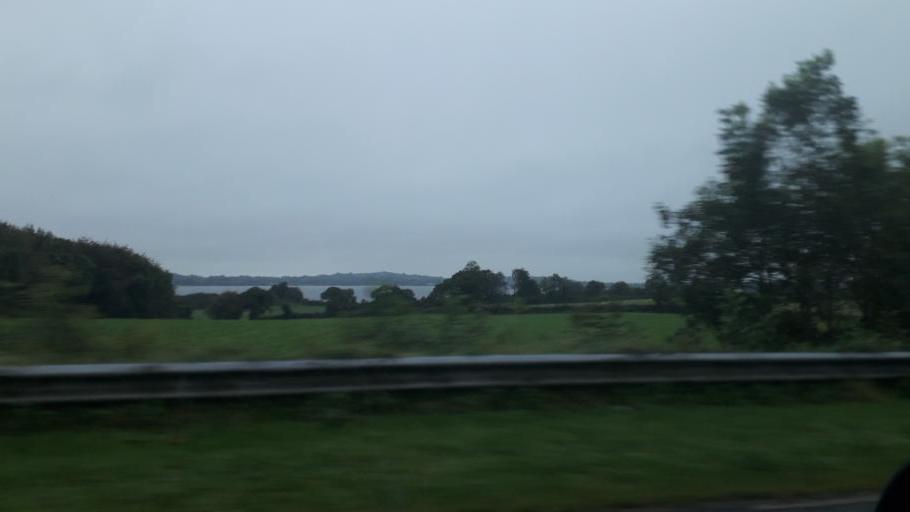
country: IE
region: Leinster
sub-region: An Iarmhi
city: An Muileann gCearr
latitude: 53.5824
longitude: -7.3699
